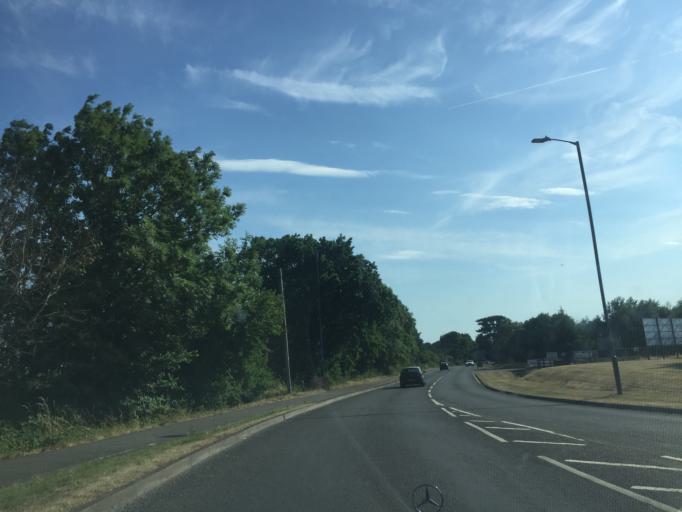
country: GB
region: England
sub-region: Warwickshire
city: Warwick
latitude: 52.2637
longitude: -1.6034
